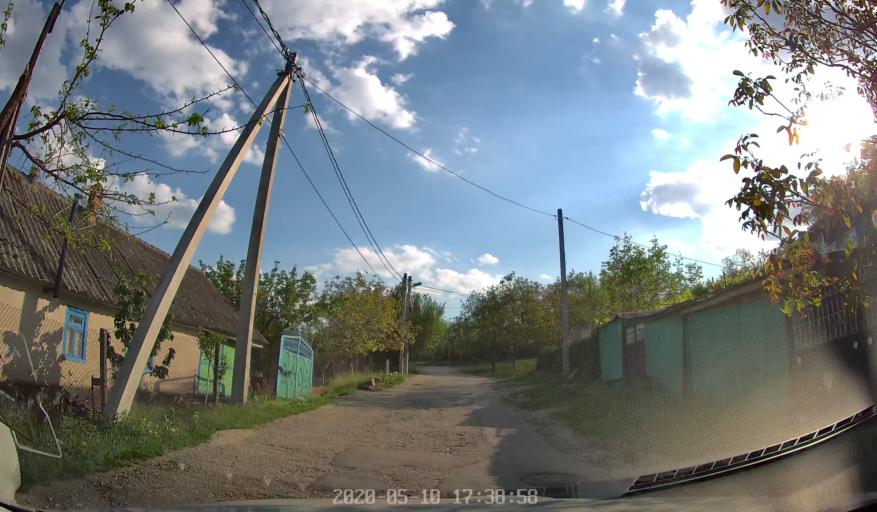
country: MD
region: Chisinau
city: Vadul lui Voda
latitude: 47.0911
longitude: 29.0704
